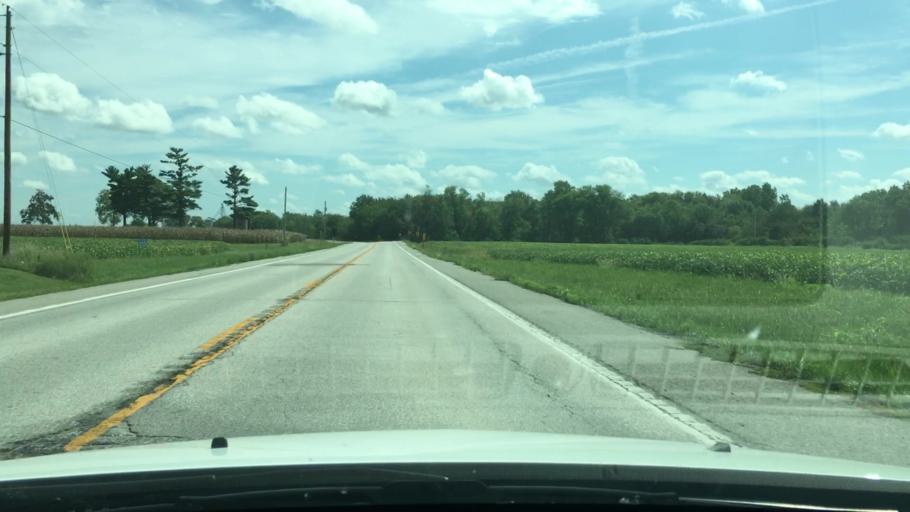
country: US
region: Missouri
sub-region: Audrain County
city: Vandalia
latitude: 39.2789
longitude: -91.5640
